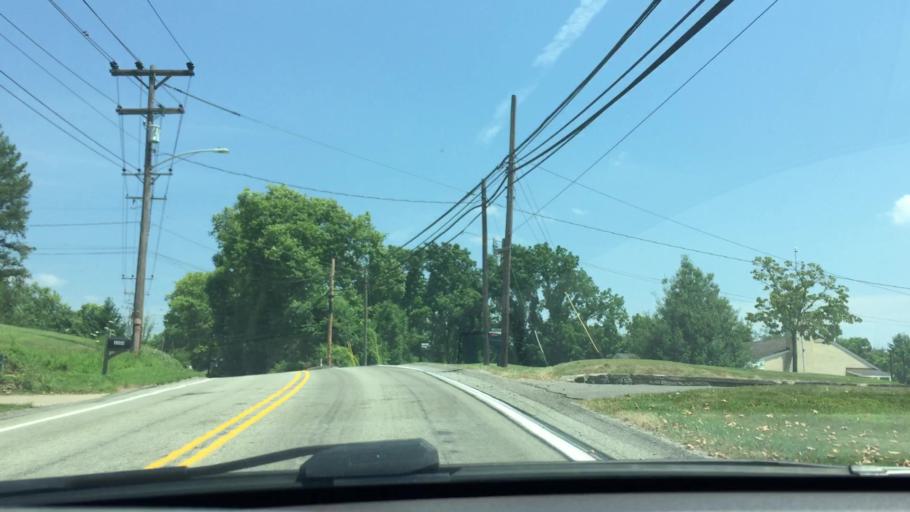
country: US
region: Pennsylvania
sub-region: Allegheny County
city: Bridgeville
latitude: 40.3307
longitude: -80.1345
